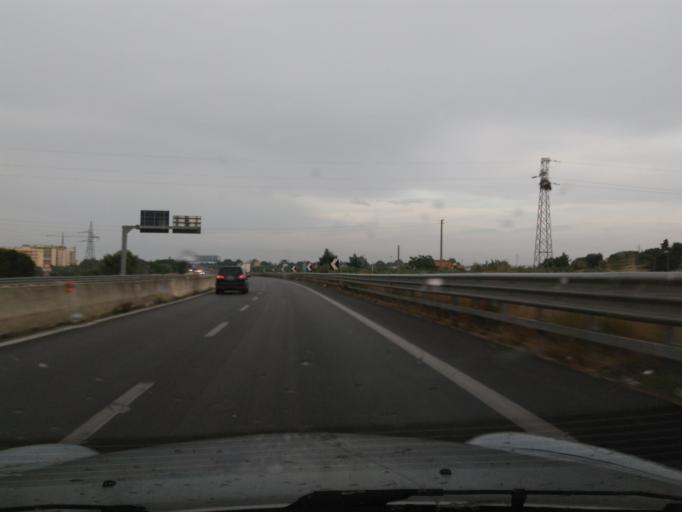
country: IT
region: Apulia
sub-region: Provincia di Bari
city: Molfetta
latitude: 41.1857
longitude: 16.5889
